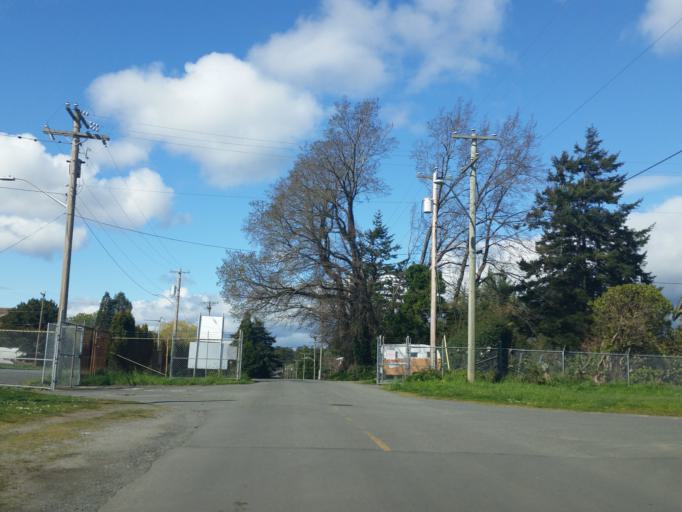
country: CA
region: British Columbia
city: Victoria
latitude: 48.4213
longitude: -123.4069
